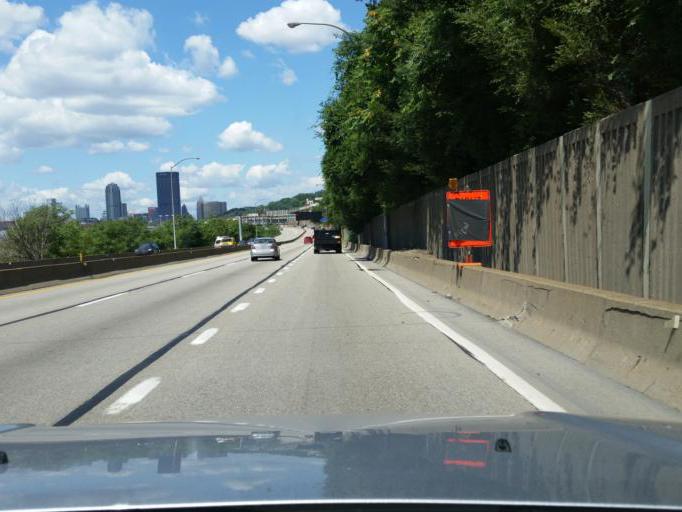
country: US
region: Pennsylvania
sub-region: Allegheny County
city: Bloomfield
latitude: 40.4333
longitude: -79.9623
